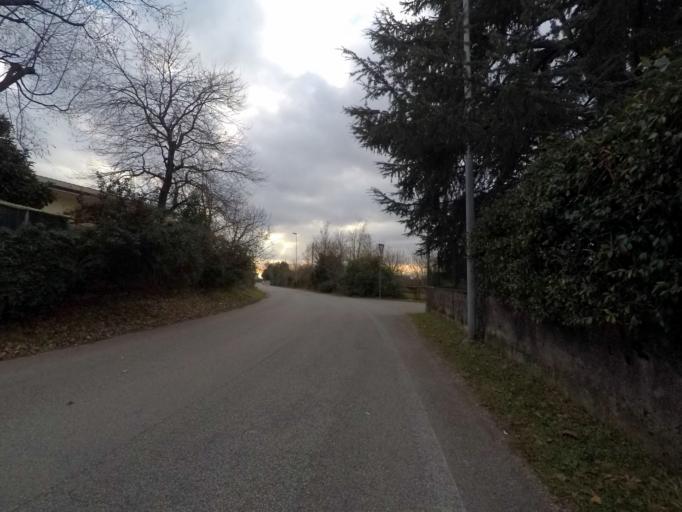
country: IT
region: Friuli Venezia Giulia
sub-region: Provincia di Udine
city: Tavagnacco
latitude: 46.1237
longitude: 13.2091
